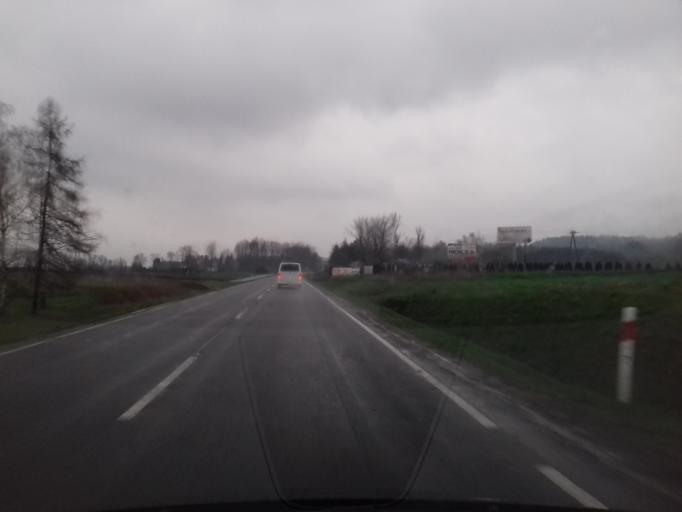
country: PL
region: Lesser Poland Voivodeship
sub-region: Powiat nowosadecki
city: Stary Sacz
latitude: 49.5563
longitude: 20.6549
